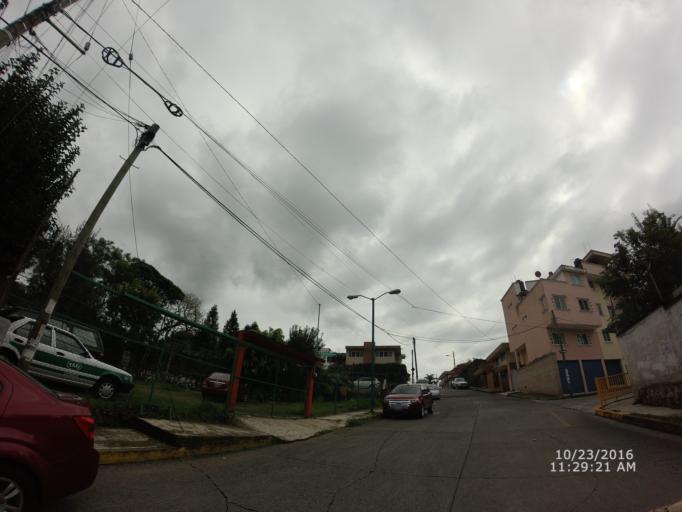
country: MX
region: Veracruz
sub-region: Tlalnelhuayocan
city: Guadalupe Victoria
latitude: 19.5488
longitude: -96.9390
